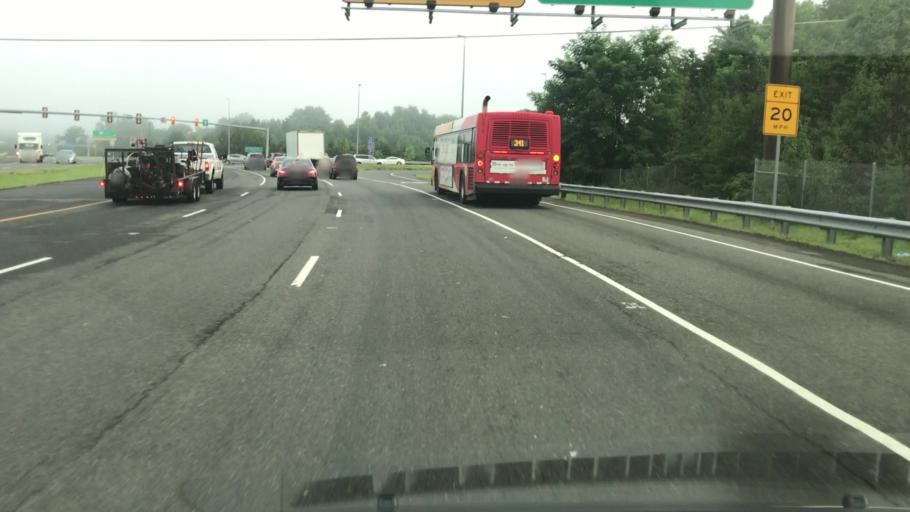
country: US
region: Virginia
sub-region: Fairfax County
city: West Springfield
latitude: 38.7576
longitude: -77.2156
